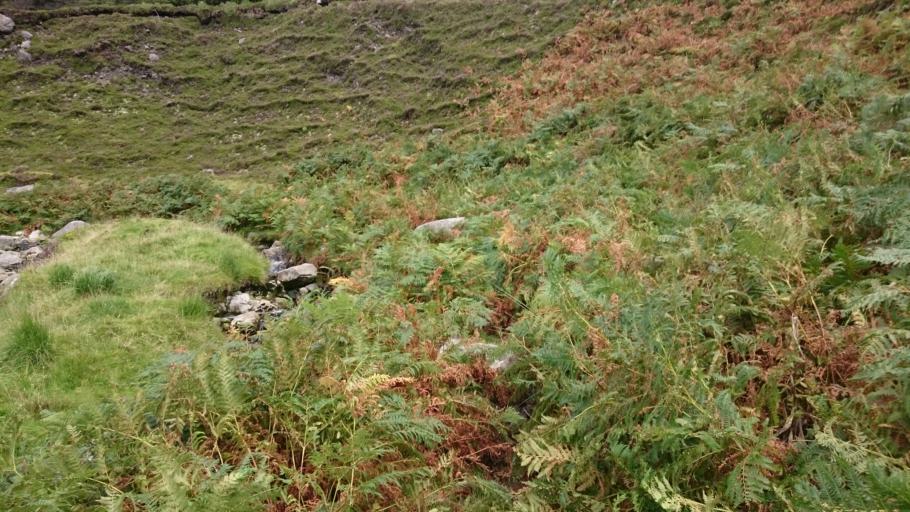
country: IE
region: Connaught
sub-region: Maigh Eo
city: Westport
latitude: 53.9890
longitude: -9.5851
